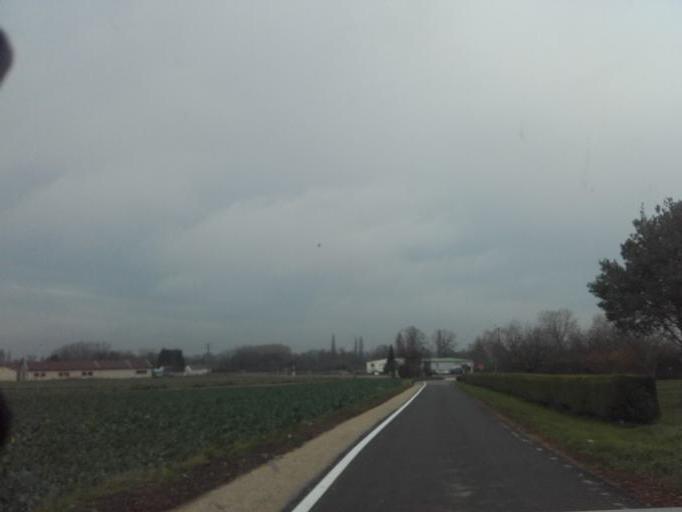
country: FR
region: Bourgogne
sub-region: Departement de la Cote-d'Or
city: Bligny-les-Beaune
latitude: 46.9925
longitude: 4.9415
